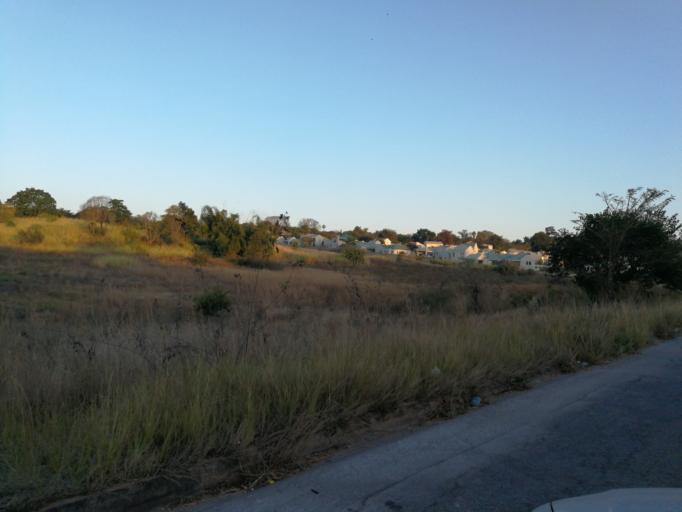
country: ZA
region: Mpumalanga
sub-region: Ehlanzeni District
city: White River
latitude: -25.3191
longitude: 31.0228
